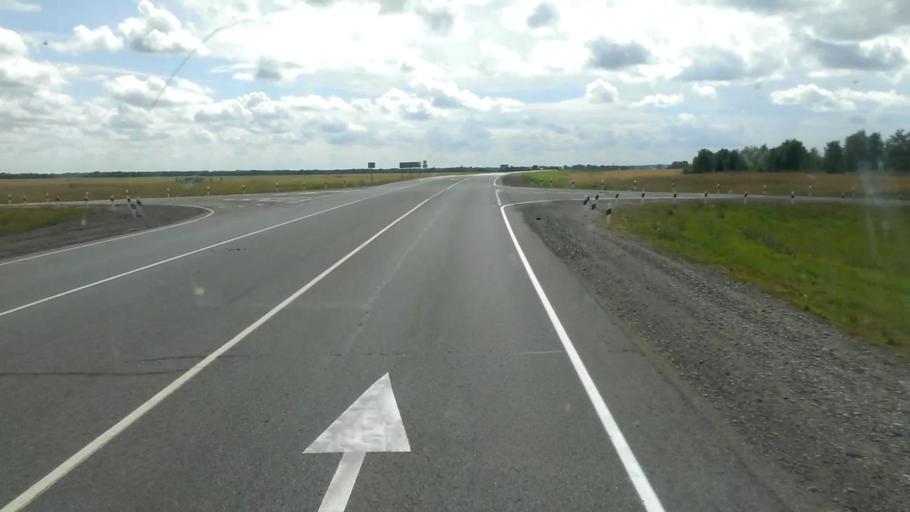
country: RU
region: Altai Krai
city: Troitskoye
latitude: 52.9084
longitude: 84.8272
